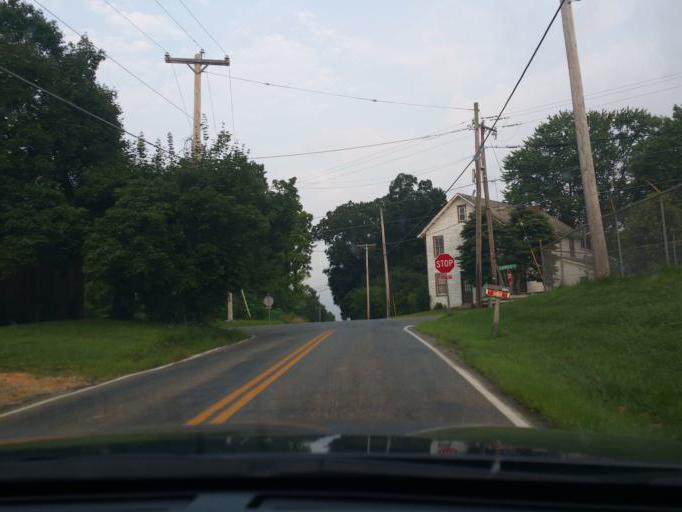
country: US
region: Maryland
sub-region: Cecil County
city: Rising Sun
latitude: 39.6990
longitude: -76.1794
